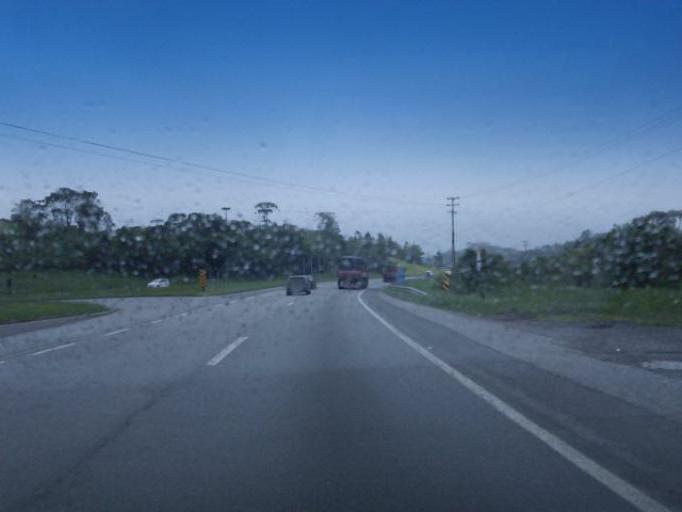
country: BR
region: Parana
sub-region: Campina Grande Do Sul
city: Campina Grande do Sul
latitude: -25.2977
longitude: -48.9391
